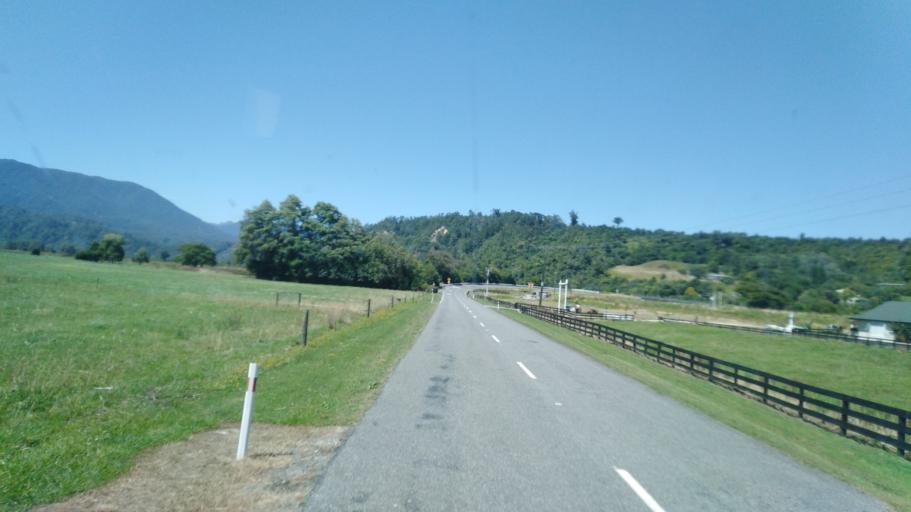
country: NZ
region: West Coast
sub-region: Buller District
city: Westport
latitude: -41.2575
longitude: 172.1315
